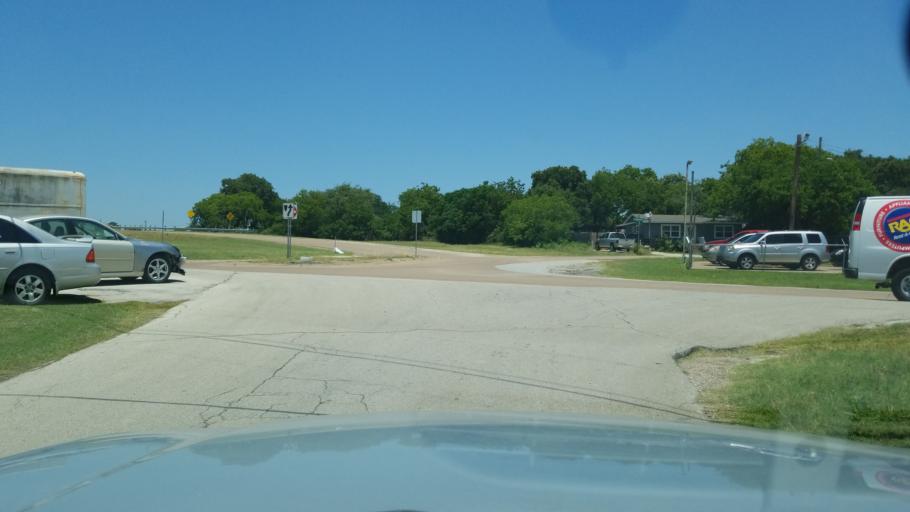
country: US
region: Texas
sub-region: Dallas County
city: Irving
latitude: 32.8056
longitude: -96.9206
